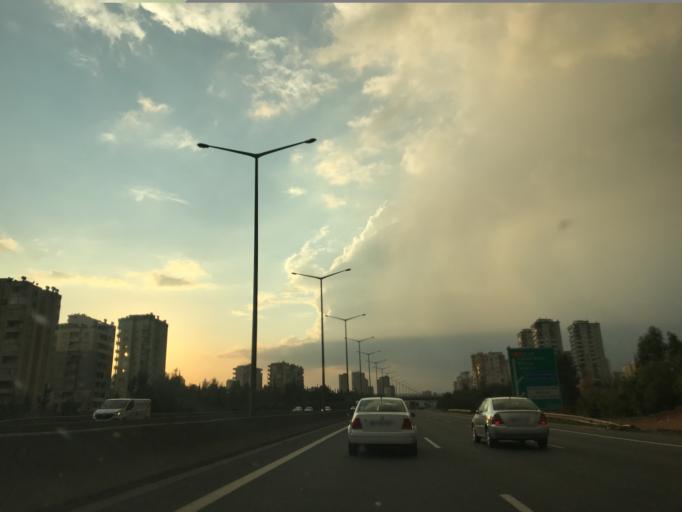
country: TR
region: Adana
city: Seyhan
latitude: 37.0304
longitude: 35.2704
